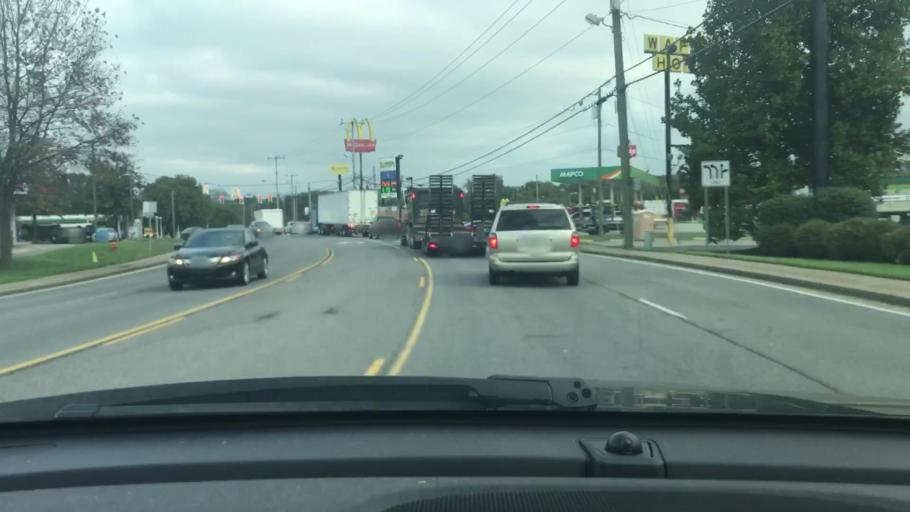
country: US
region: Tennessee
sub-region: Davidson County
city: Goodlettsville
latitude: 36.3241
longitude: -86.7011
